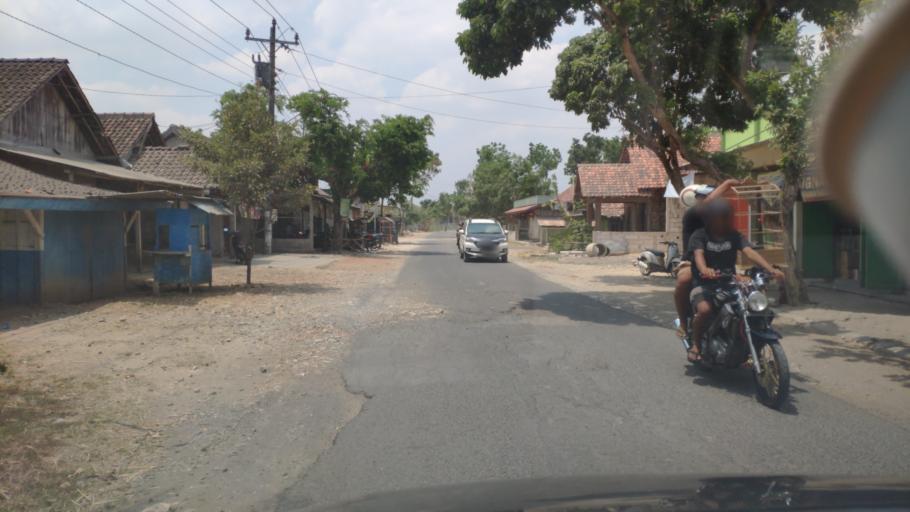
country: ID
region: Central Java
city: Boto
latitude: -7.0056
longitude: 111.3922
